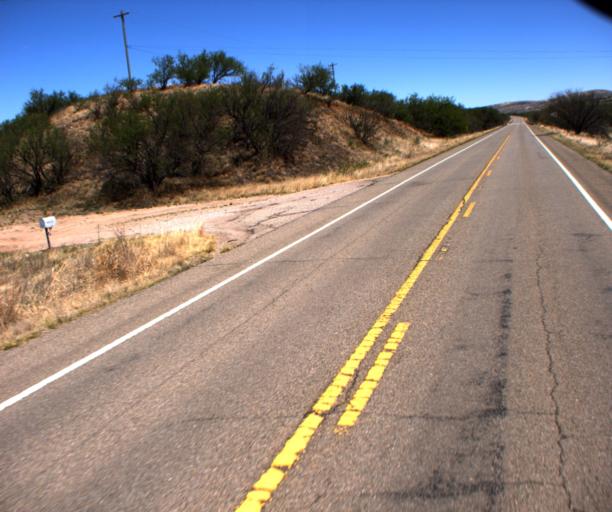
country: US
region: Arizona
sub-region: Santa Cruz County
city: Rio Rico
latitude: 31.5926
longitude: -110.7255
